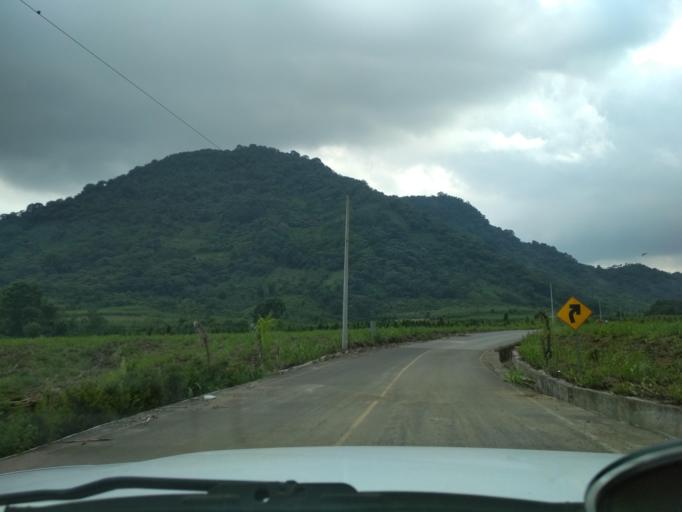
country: MX
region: Veracruz
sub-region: Fortin
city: Santa Lucia Potrerillo
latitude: 18.9466
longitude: -97.0610
